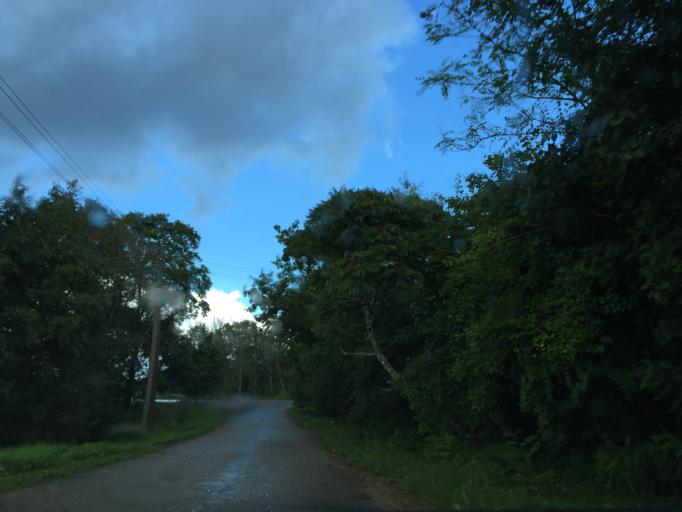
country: LV
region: Talsu Rajons
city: Sabile
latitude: 57.0516
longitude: 22.4760
